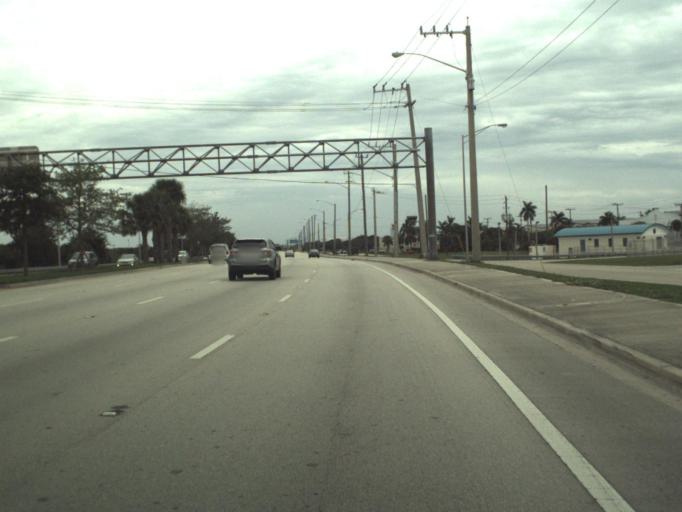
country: US
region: Florida
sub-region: Palm Beach County
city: Haverhill
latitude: 26.6774
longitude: -80.0908
